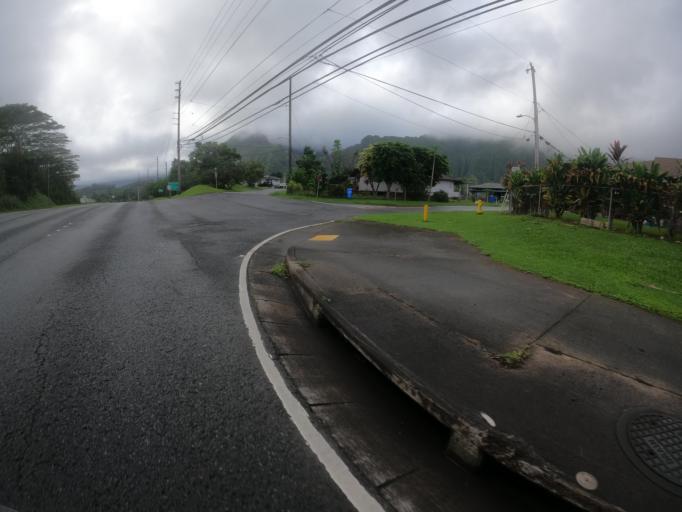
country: US
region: Hawaii
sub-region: Honolulu County
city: Kane'ohe
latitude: 21.3884
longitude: -157.7941
